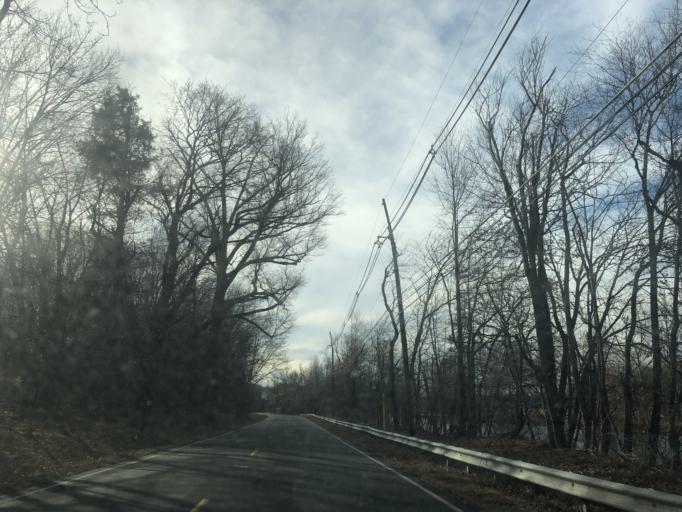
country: US
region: New Jersey
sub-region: Somerset County
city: Kingston
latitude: 40.3504
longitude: -74.6259
